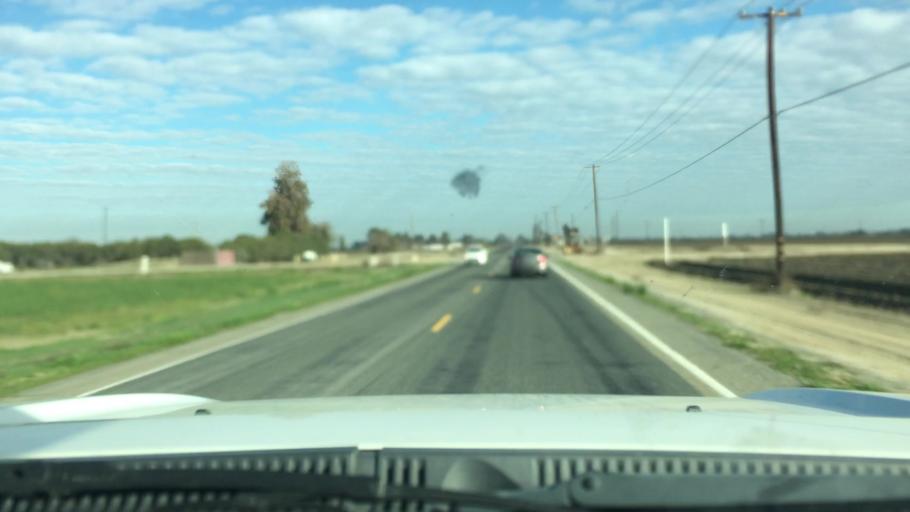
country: US
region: California
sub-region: Kings County
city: Stratford
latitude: 36.2178
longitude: -119.7803
